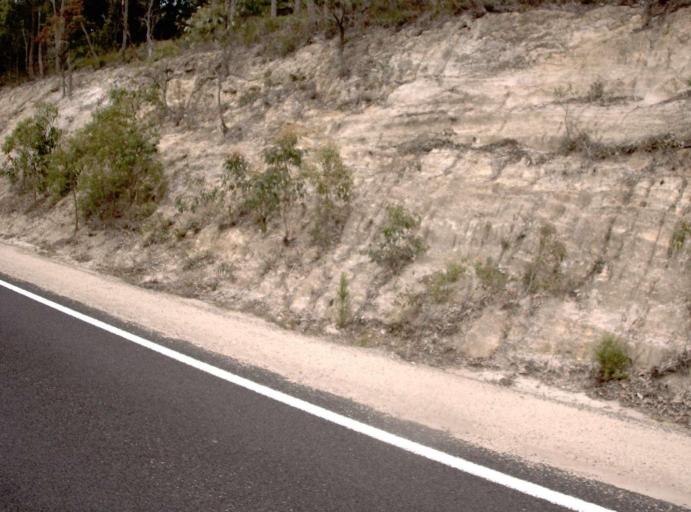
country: AU
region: New South Wales
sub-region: Bega Valley
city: Eden
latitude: -37.4043
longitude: 149.6658
